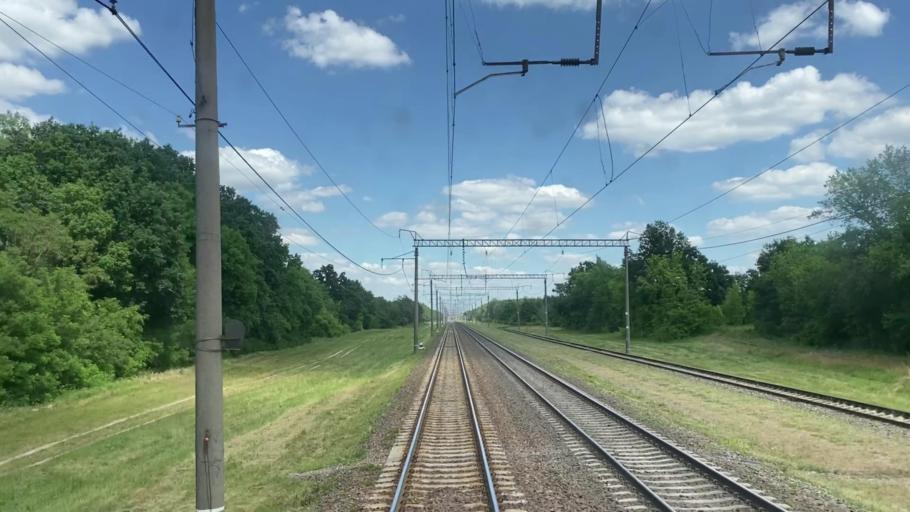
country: BY
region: Brest
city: Brest
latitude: 52.1221
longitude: 23.7811
